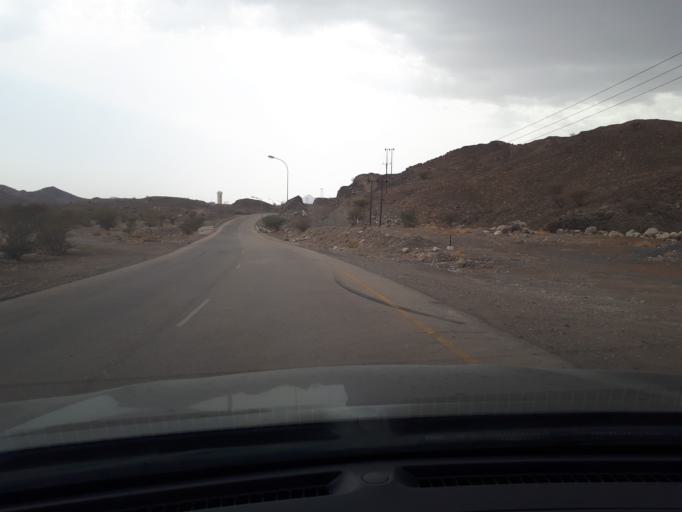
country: OM
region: Ash Sharqiyah
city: Badiyah
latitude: 22.5668
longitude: 59.0527
